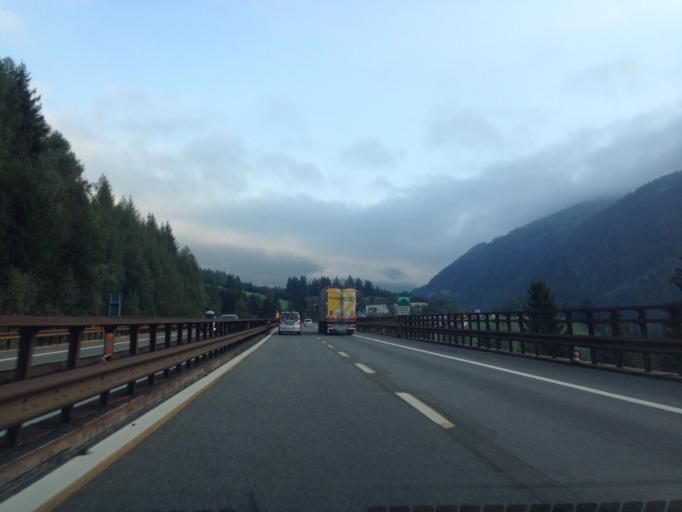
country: IT
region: Trentino-Alto Adige
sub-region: Bolzano
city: Brennero - Brenner
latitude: 46.9225
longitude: 11.4432
